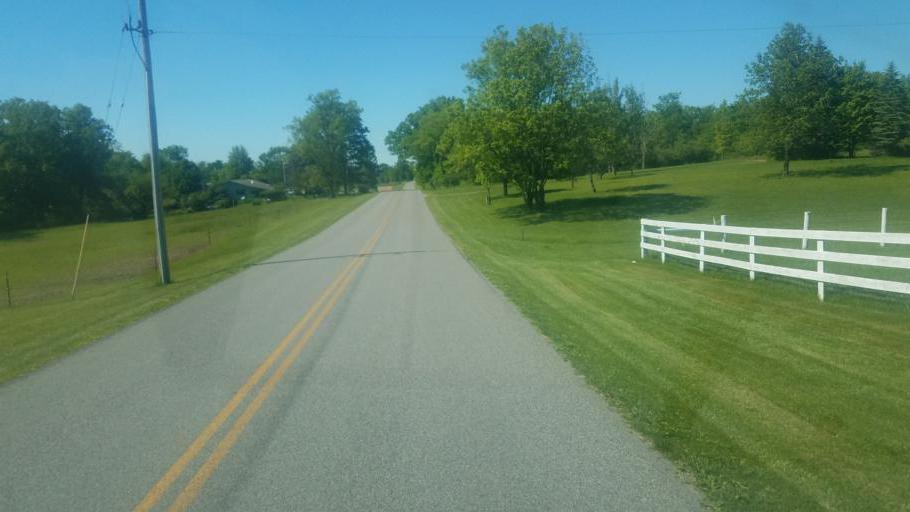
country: US
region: Ohio
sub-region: Logan County
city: Northwood
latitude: 40.4451
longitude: -83.7181
